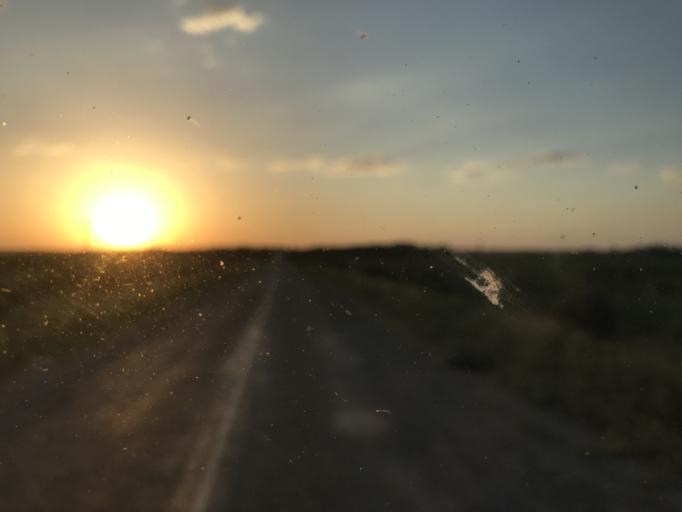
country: UZ
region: Toshkent
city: Yangiyul
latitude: 41.3832
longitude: 68.7736
